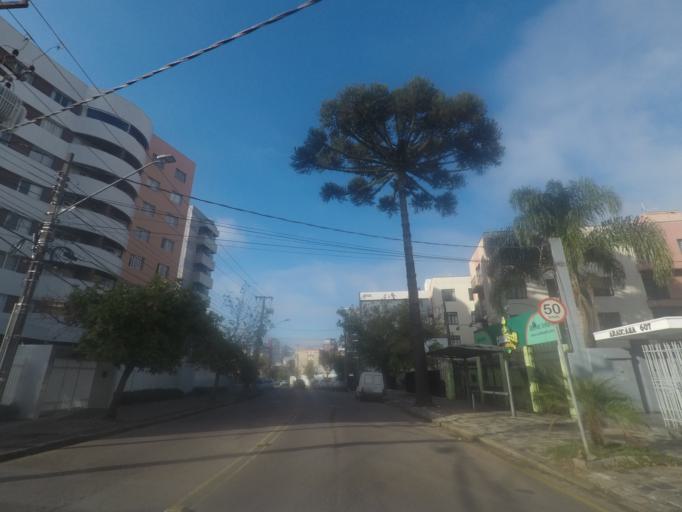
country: BR
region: Parana
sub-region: Curitiba
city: Curitiba
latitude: -25.4098
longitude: -49.2644
